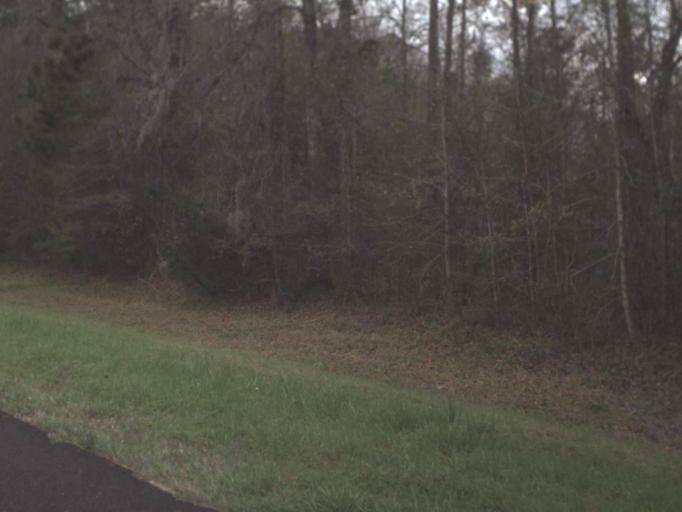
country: US
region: Florida
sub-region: Leon County
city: Tallahassee
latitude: 30.6368
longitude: -84.1692
